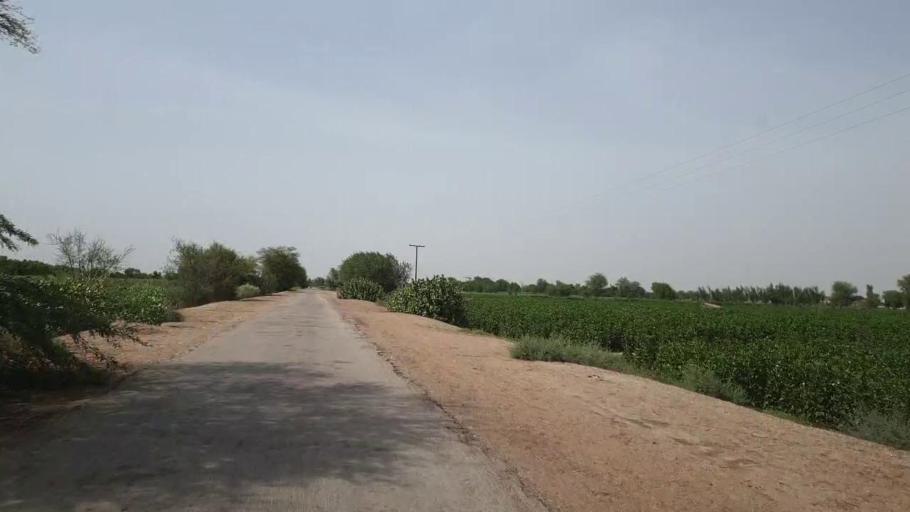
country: PK
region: Sindh
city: Daur
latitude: 26.5318
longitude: 68.4075
